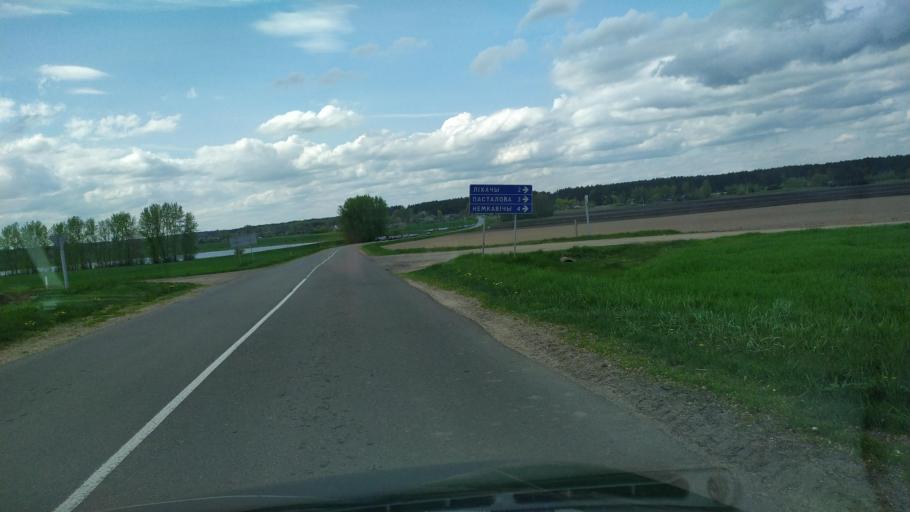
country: BY
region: Brest
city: Pruzhany
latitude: 52.6725
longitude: 24.3717
